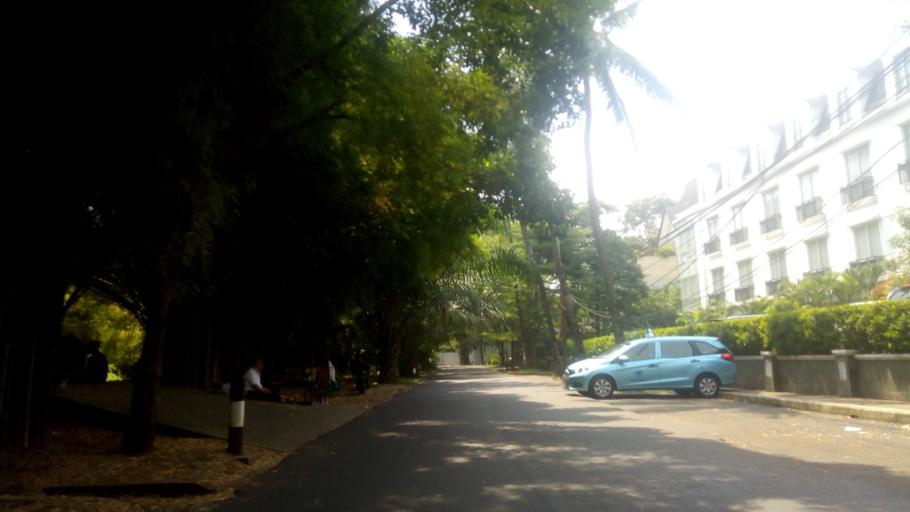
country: ID
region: Jakarta Raya
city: Jakarta
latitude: -6.2381
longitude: 106.8355
